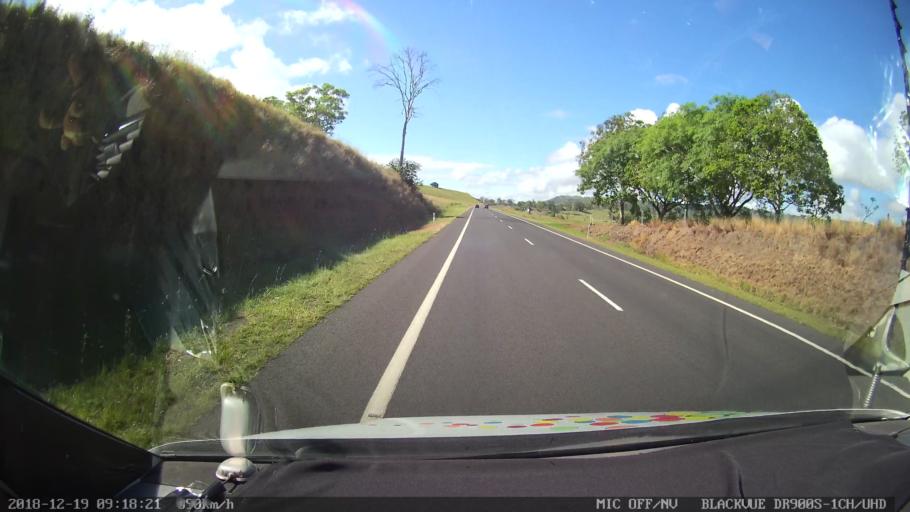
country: AU
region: New South Wales
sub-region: Kyogle
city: Kyogle
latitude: -28.5459
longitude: 152.9772
